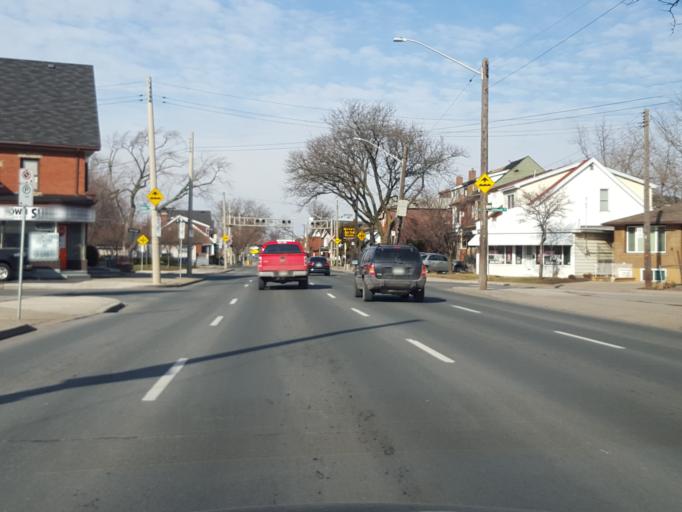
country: CA
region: Ontario
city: Hamilton
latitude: 43.2457
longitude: -79.8263
